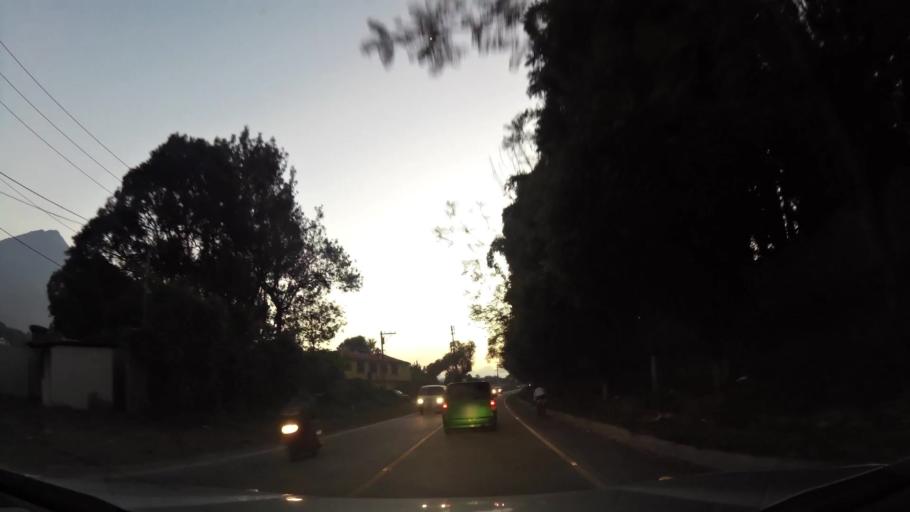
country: GT
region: Sacatepequez
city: Ciudad Vieja
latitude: 14.5321
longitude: -90.7505
